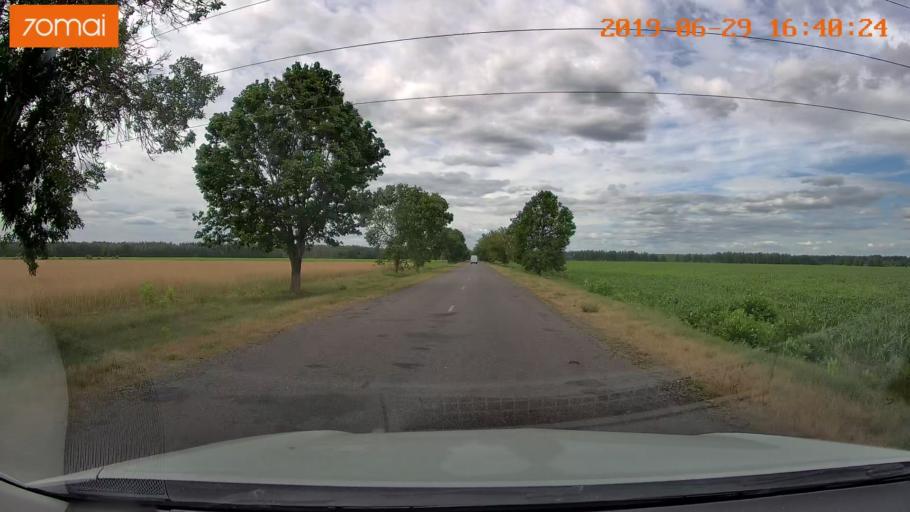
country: BY
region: Brest
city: Luninyets
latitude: 52.2554
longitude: 27.0172
